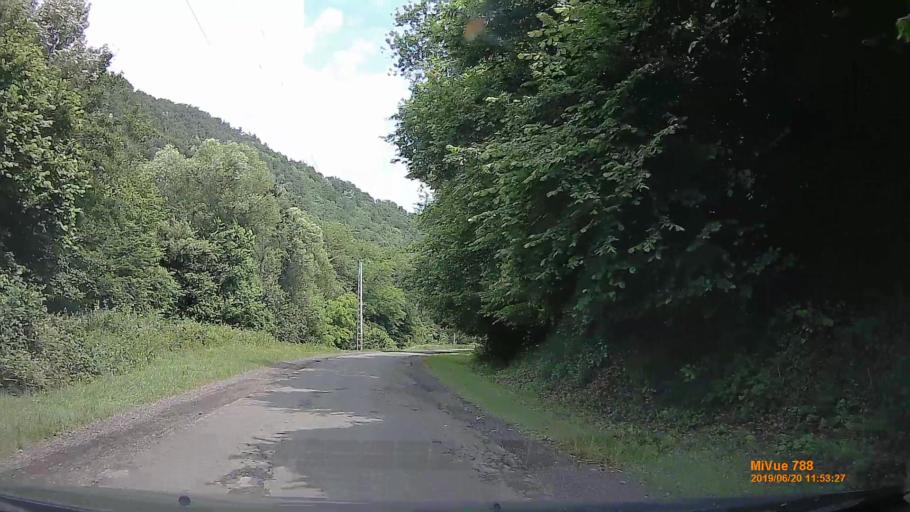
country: HU
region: Baranya
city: Mecseknadasd
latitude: 46.2229
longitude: 18.4288
